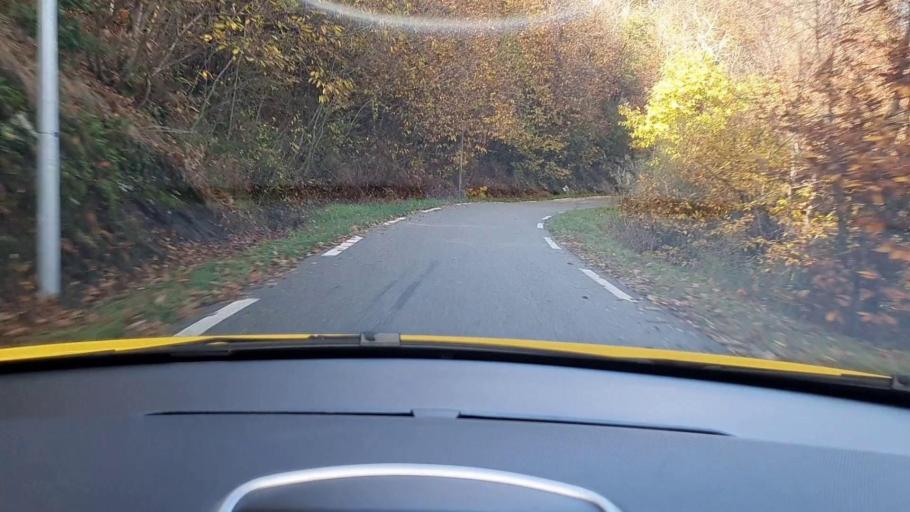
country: FR
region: Languedoc-Roussillon
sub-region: Departement du Gard
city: Valleraugue
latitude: 44.1632
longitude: 3.6518
